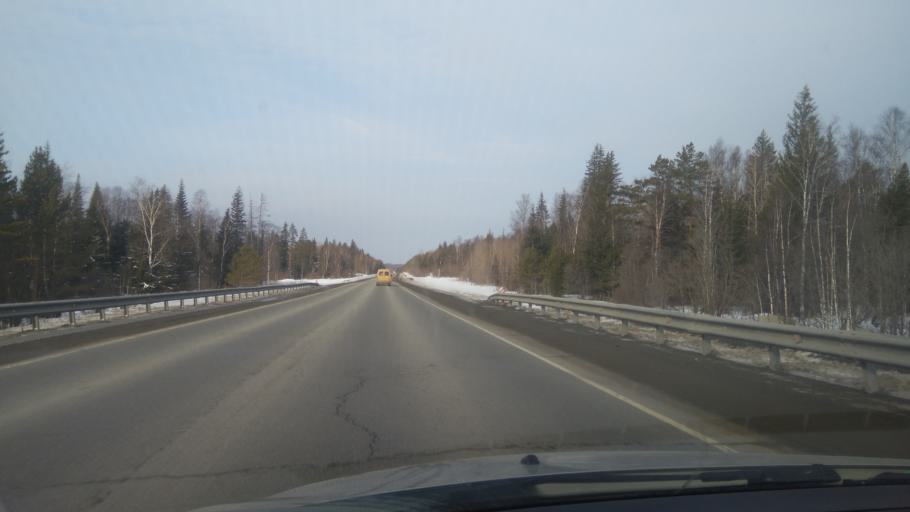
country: RU
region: Sverdlovsk
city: Nizhniye Sergi
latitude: 56.8239
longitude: 59.2958
